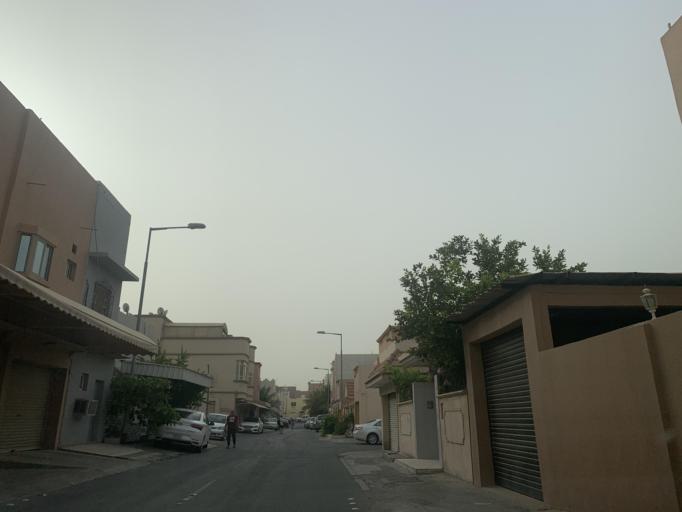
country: BH
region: Northern
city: Madinat `Isa
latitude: 26.1618
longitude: 50.5659
